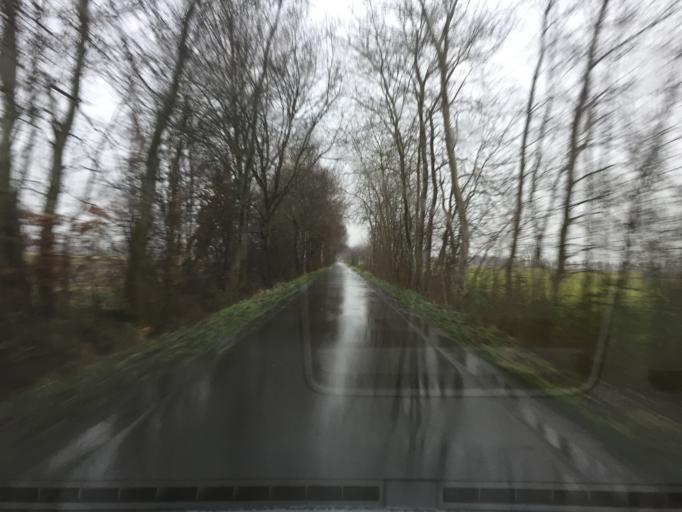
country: DE
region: Lower Saxony
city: Sulingen
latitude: 52.6515
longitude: 8.8342
